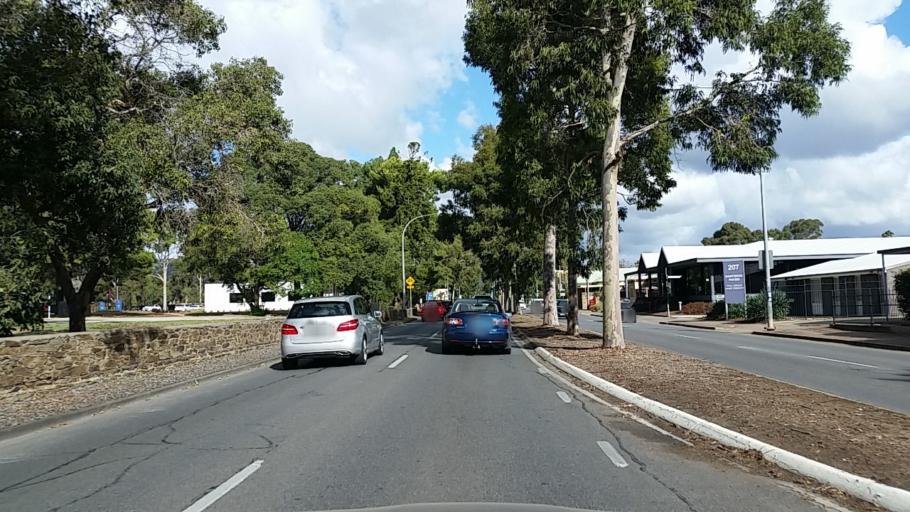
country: AU
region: South Australia
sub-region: Unley
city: Fullarton
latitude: -34.9416
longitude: 138.6247
